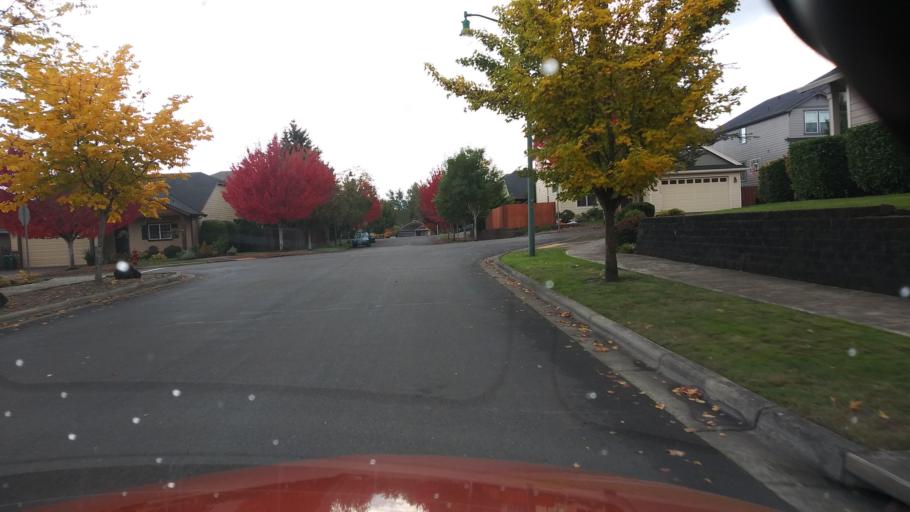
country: US
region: Oregon
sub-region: Washington County
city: Forest Grove
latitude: 45.5390
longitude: -123.1287
